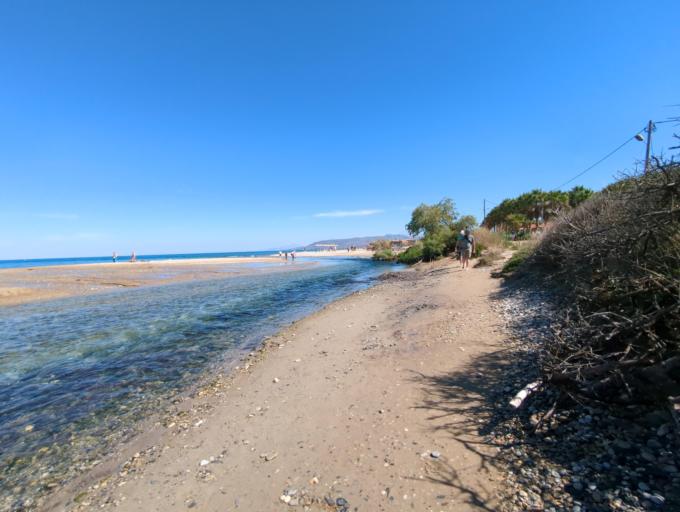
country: GR
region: Crete
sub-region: Nomos Chanias
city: Georgioupolis
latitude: 35.3597
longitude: 24.2662
